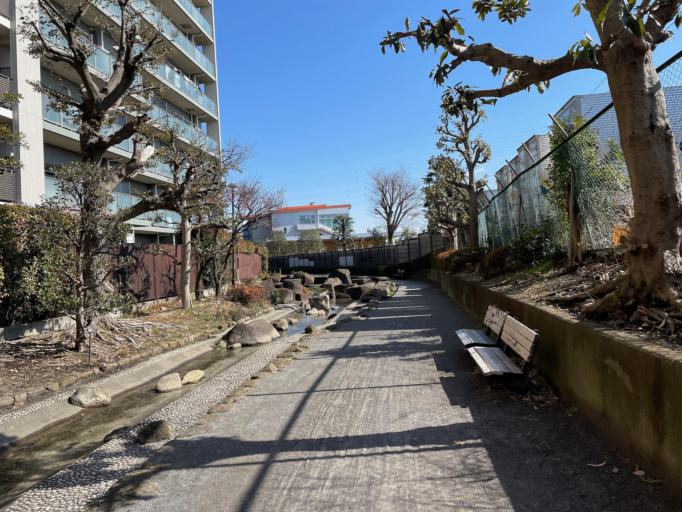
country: JP
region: Tokyo
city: Kokubunji
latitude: 35.6575
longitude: 139.4931
